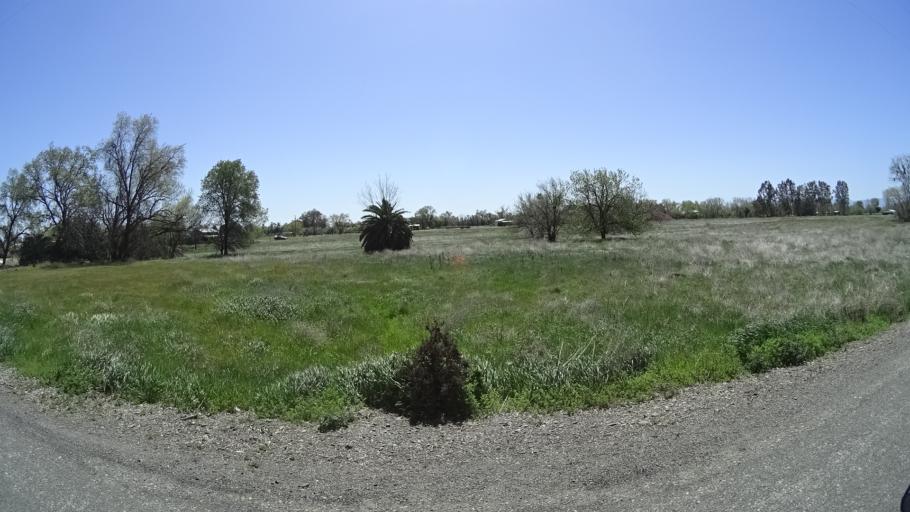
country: US
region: California
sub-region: Glenn County
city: Orland
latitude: 39.7768
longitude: -122.2414
